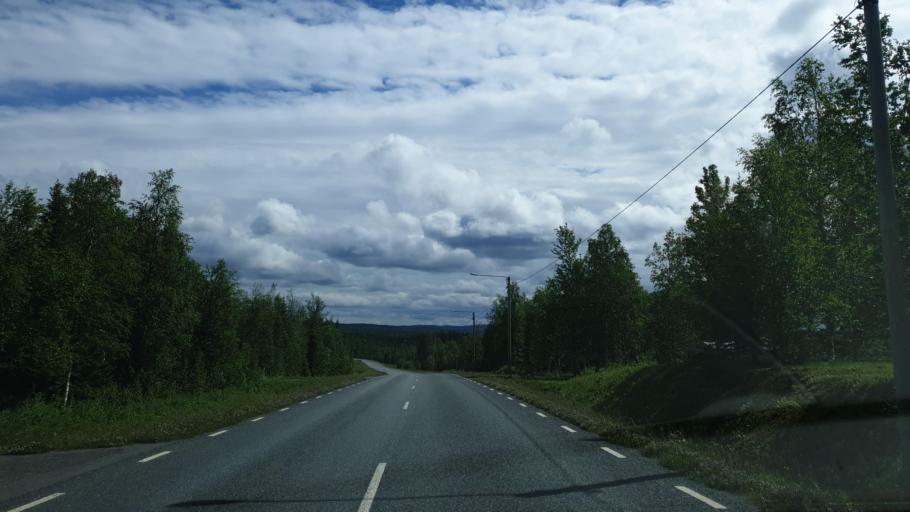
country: SE
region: Vaesterbotten
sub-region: Vilhelmina Kommun
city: Sjoberg
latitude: 65.2527
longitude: 15.5372
